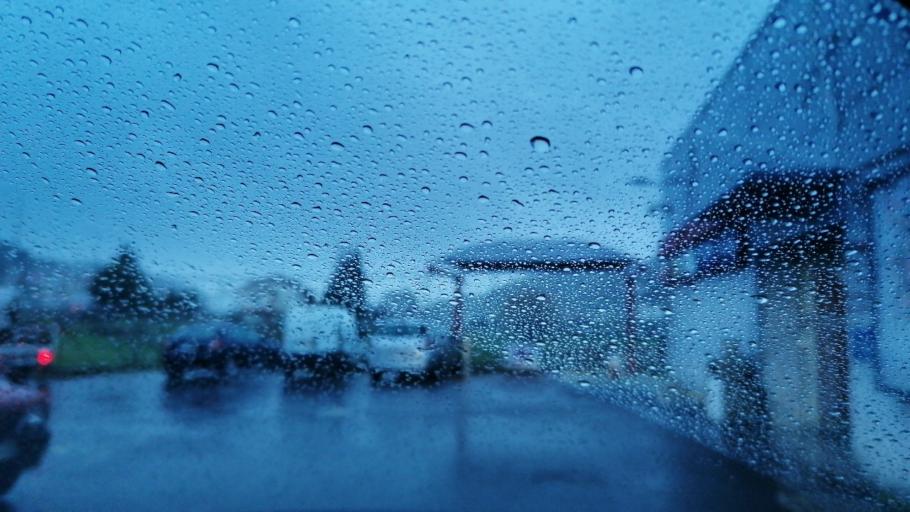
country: PT
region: Vila Real
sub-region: Vila Pouca de Aguiar
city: Vila Pouca de Aguiar
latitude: 41.4928
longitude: -7.6458
